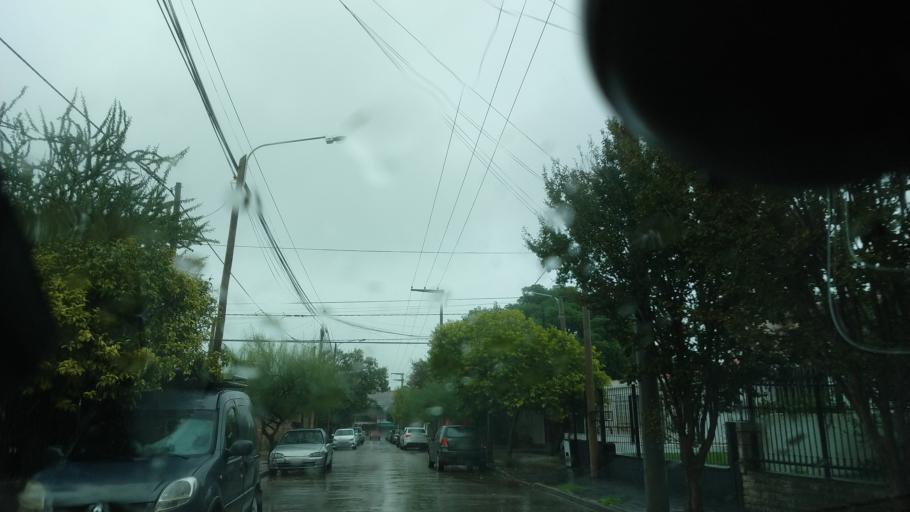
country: AR
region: Cordoba
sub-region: Departamento de Capital
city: Cordoba
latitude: -31.3673
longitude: -64.2323
